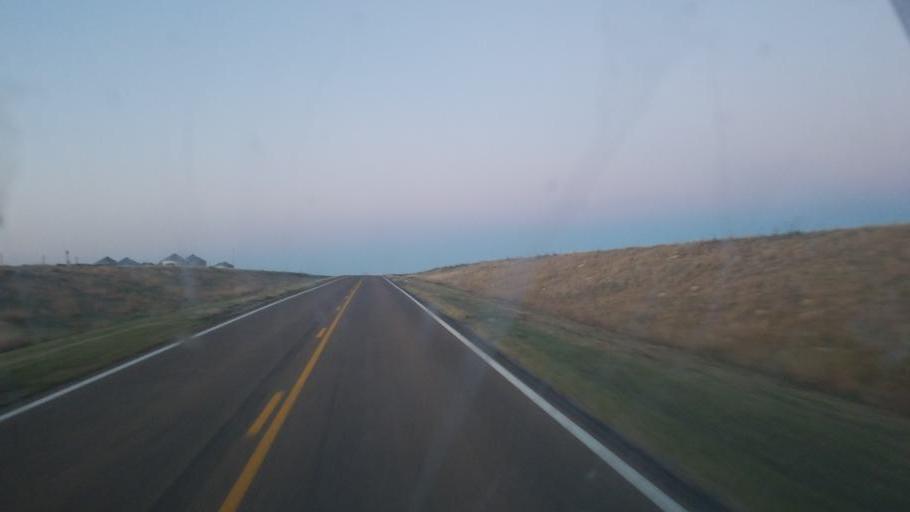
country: US
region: Kansas
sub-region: Wallace County
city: Sharon Springs
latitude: 38.9646
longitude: -101.4589
